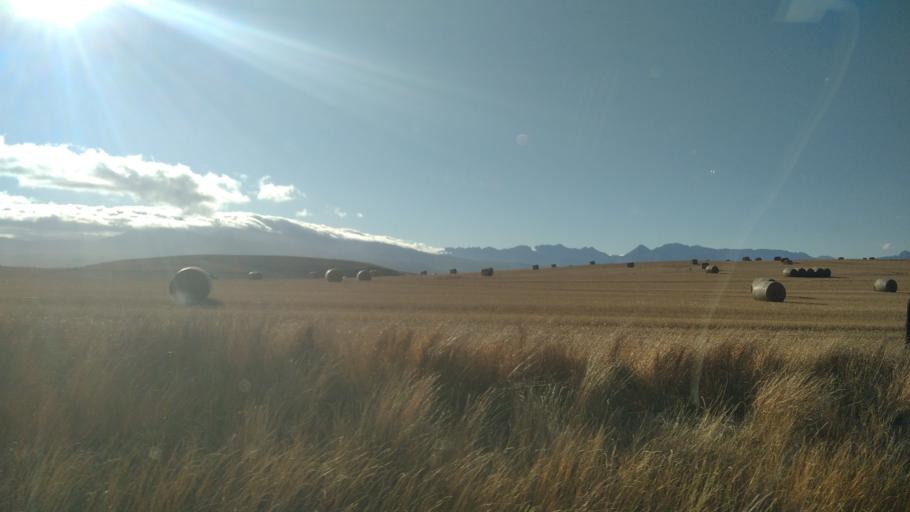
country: ZA
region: Western Cape
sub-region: Overberg District Municipality
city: Caledon
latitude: -34.1391
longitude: 19.2962
